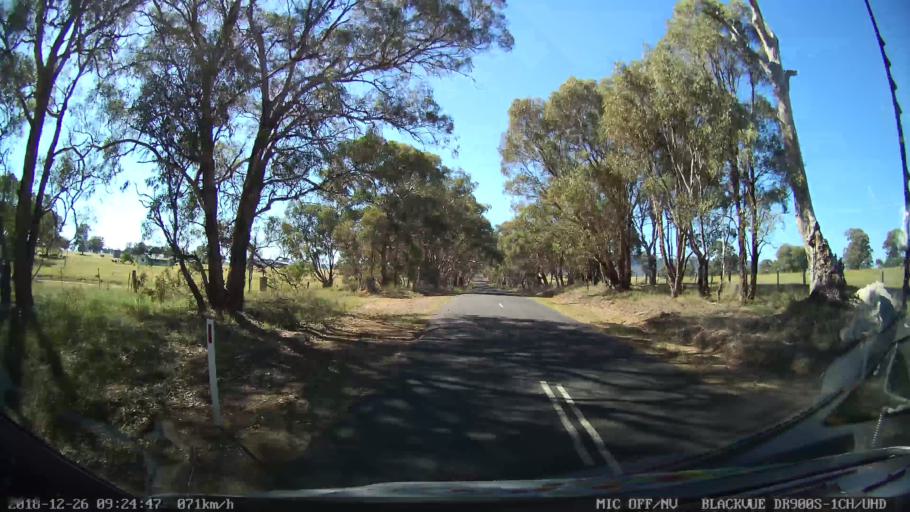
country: AU
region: New South Wales
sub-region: Mid-Western Regional
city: Kandos
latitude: -32.8135
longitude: 150.0009
